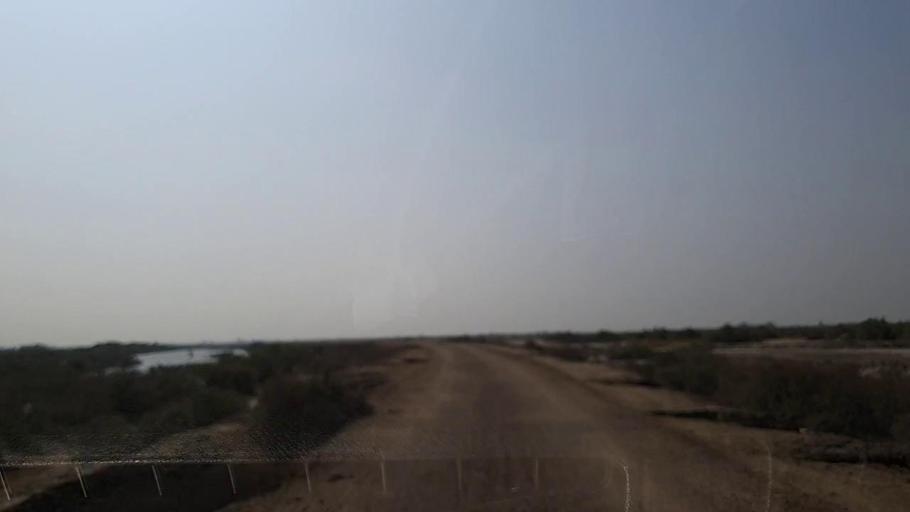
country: PK
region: Sindh
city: Gharo
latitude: 24.6804
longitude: 67.7354
